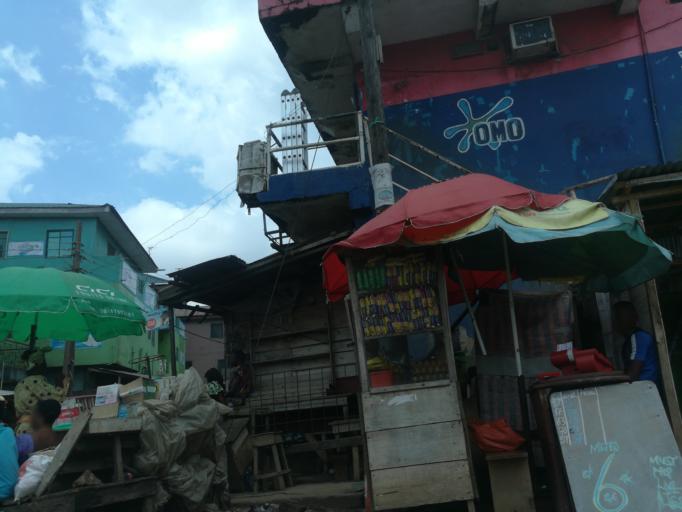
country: NG
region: Lagos
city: Mushin
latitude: 6.5293
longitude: 3.3568
